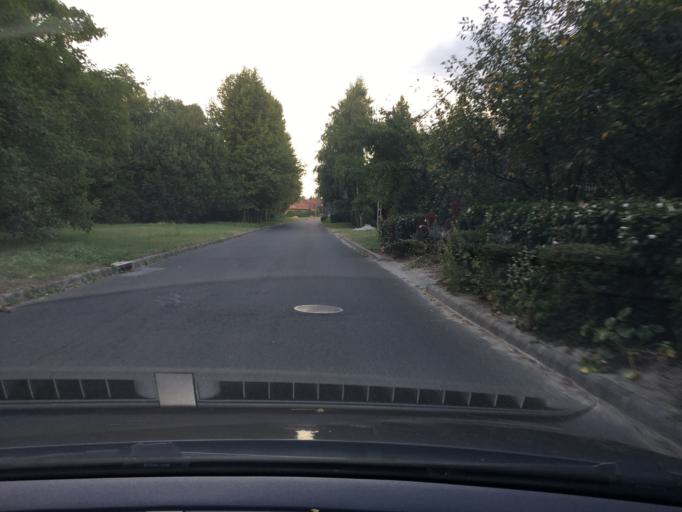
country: HU
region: Pest
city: Veresegyhaz
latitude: 47.6457
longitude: 19.3032
